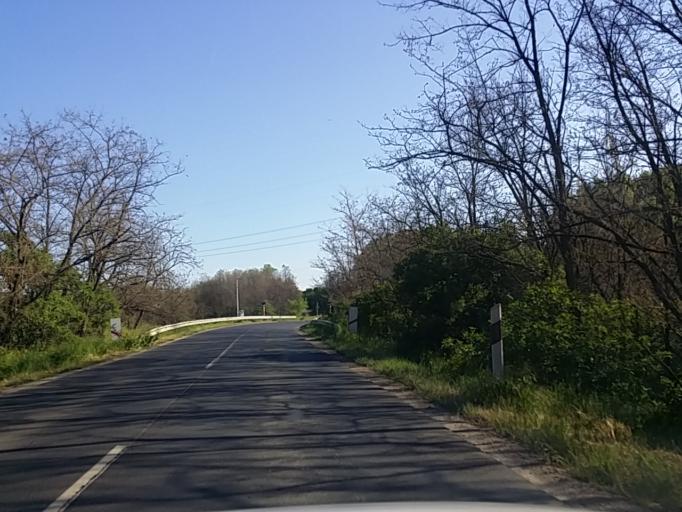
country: HU
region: Pest
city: Fot
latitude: 47.6270
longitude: 19.1990
